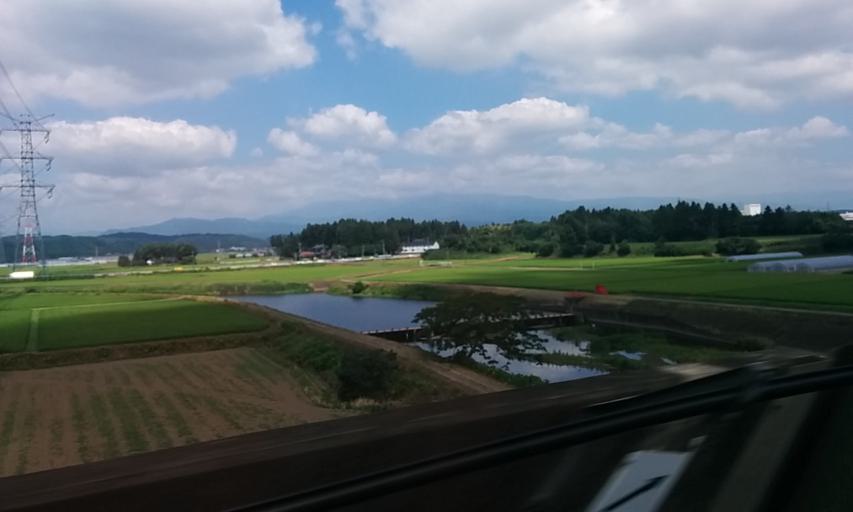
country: JP
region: Tochigi
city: Yaita
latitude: 36.7768
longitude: 139.9505
